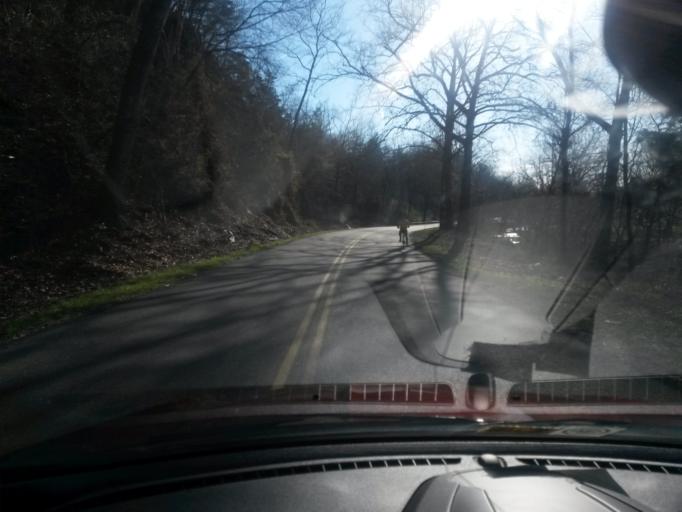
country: US
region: Virginia
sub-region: City of Lexington
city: Lexington
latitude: 37.8675
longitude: -79.5430
